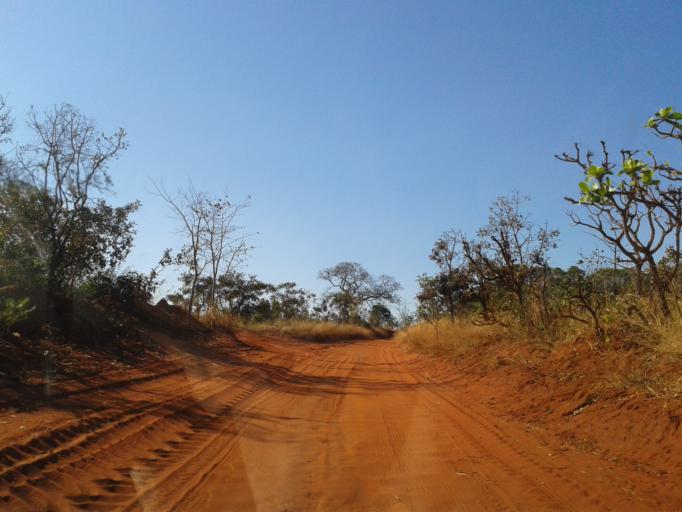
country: BR
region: Minas Gerais
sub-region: Ituiutaba
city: Ituiutaba
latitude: -19.0063
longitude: -49.3648
